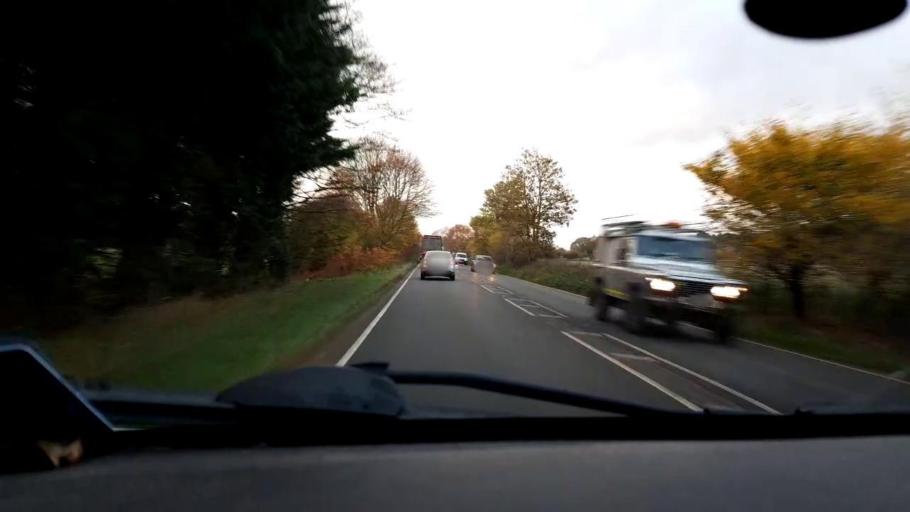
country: GB
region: England
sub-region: Norfolk
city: Costessey
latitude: 52.6977
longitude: 1.1649
